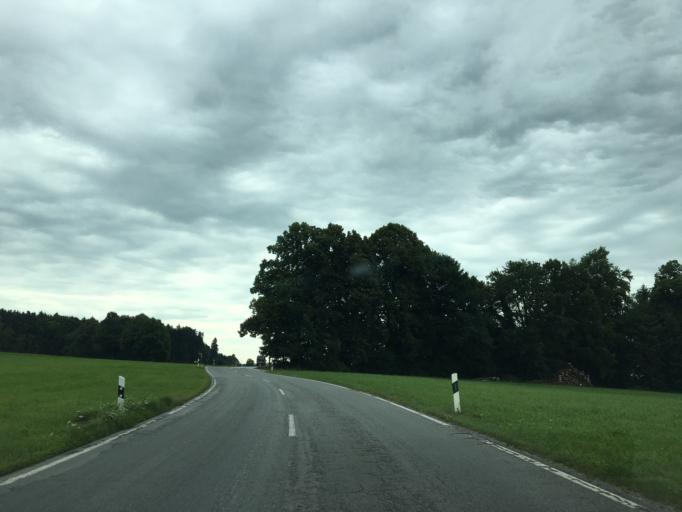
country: DE
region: Bavaria
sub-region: Upper Bavaria
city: Bad Feilnbach
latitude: 47.7673
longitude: 12.0309
